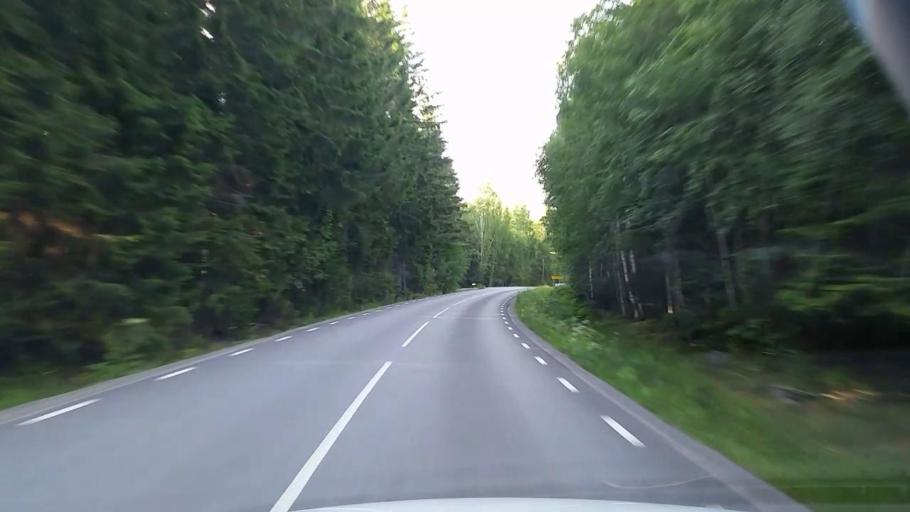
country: SE
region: Vaestmanland
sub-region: Kopings Kommun
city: Kolsva
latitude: 59.6422
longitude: 15.8235
